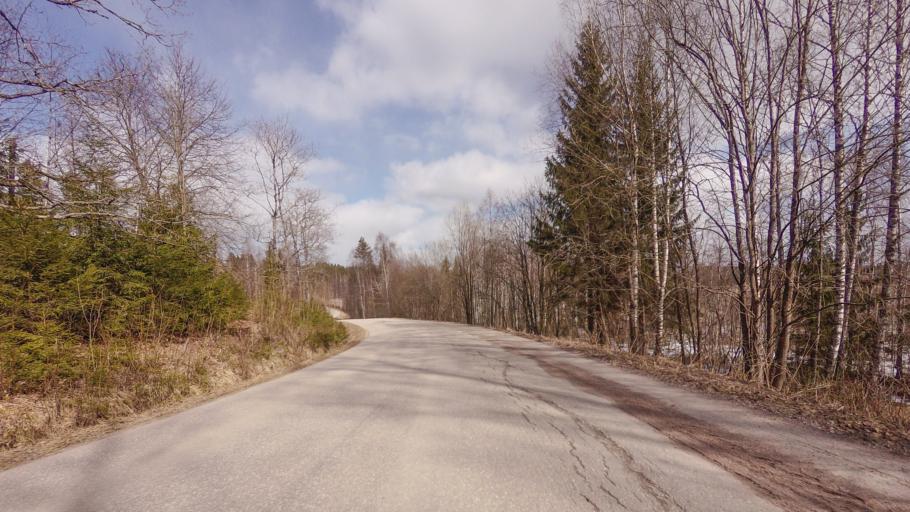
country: FI
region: Varsinais-Suomi
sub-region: Salo
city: Suomusjaervi
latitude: 60.3158
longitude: 23.6445
